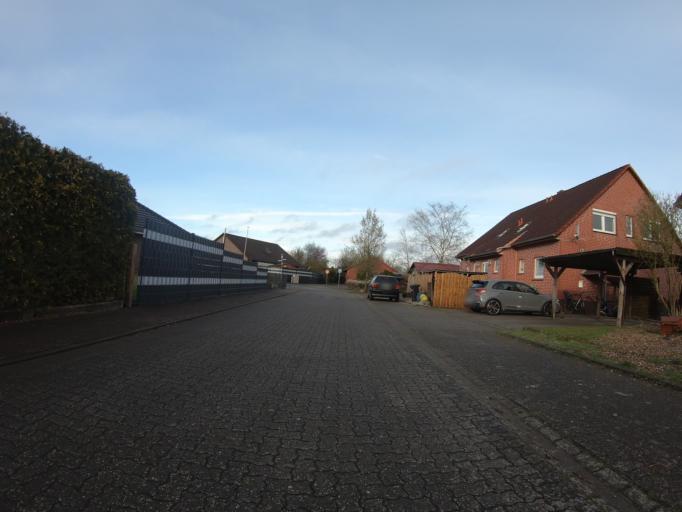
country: DE
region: Lower Saxony
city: Wesendorf
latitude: 52.5996
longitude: 10.5422
